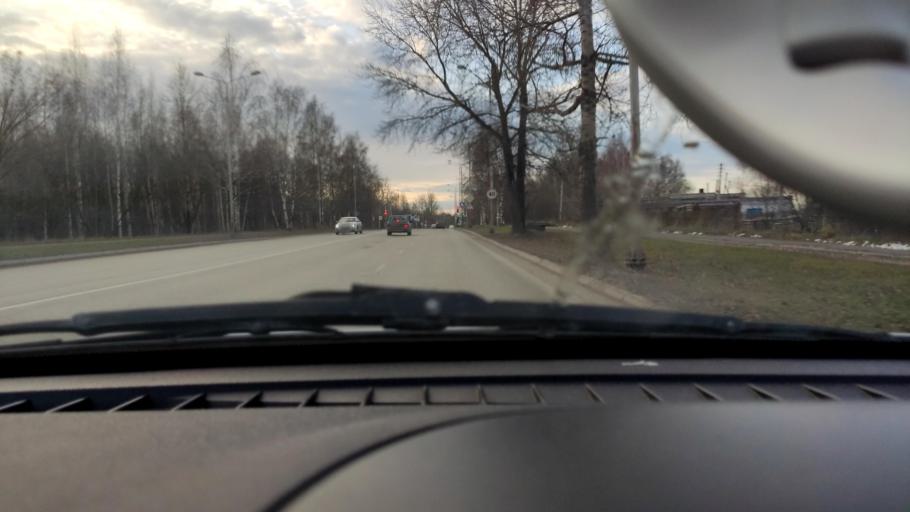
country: RU
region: Perm
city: Perm
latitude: 58.0941
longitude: 56.3838
